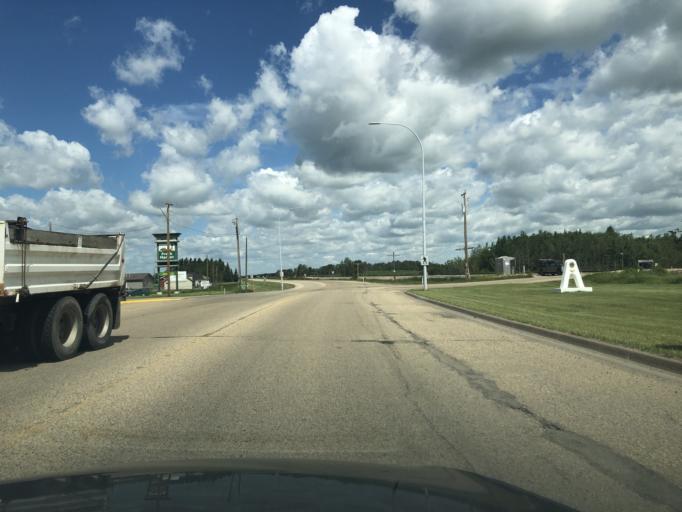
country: CA
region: Alberta
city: Millet
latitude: 53.0971
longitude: -113.4726
